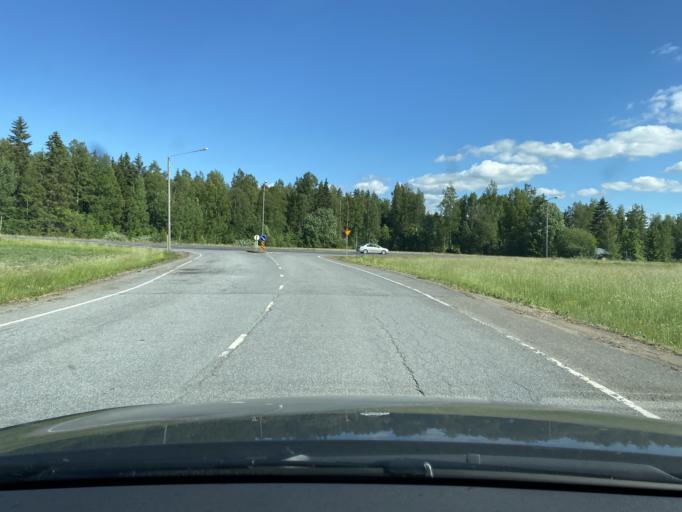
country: FI
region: Satakunta
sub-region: Pori
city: Huittinen
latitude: 61.1757
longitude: 22.7102
